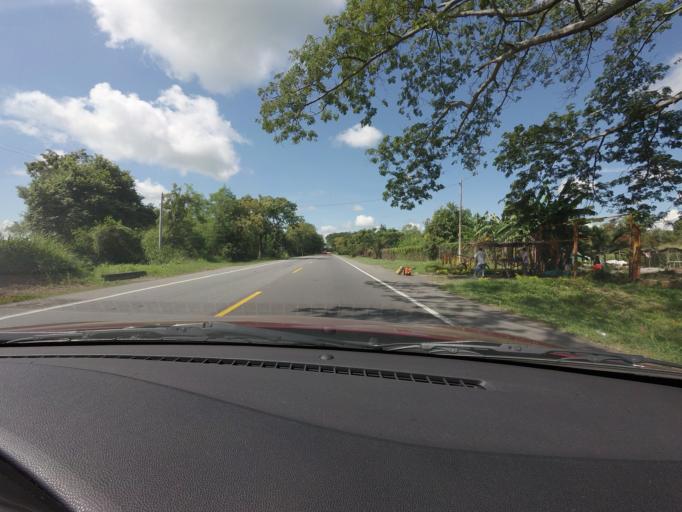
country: CO
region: Tolima
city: Espinal
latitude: 4.1669
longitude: -74.9136
